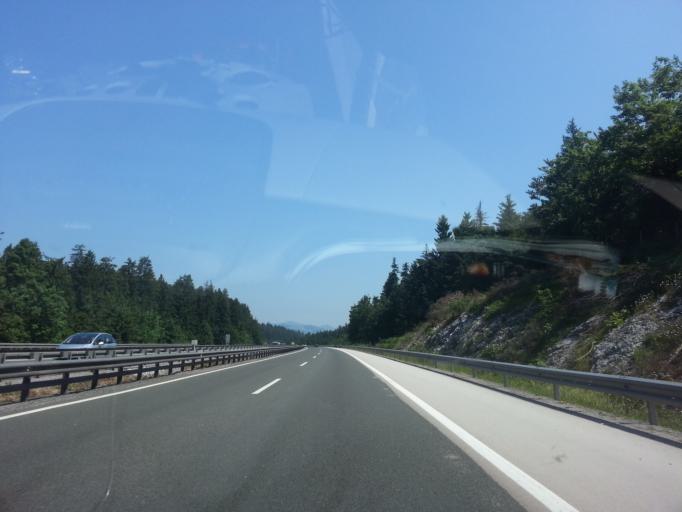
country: SI
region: Logatec
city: Logatec
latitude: 45.9240
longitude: 14.2688
